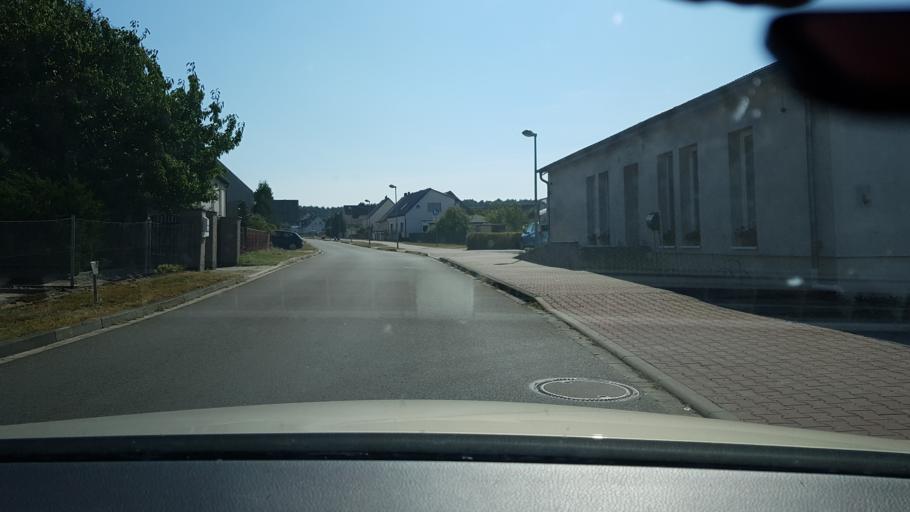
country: DE
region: Brandenburg
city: Gross Lindow
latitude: 52.1424
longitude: 14.5335
